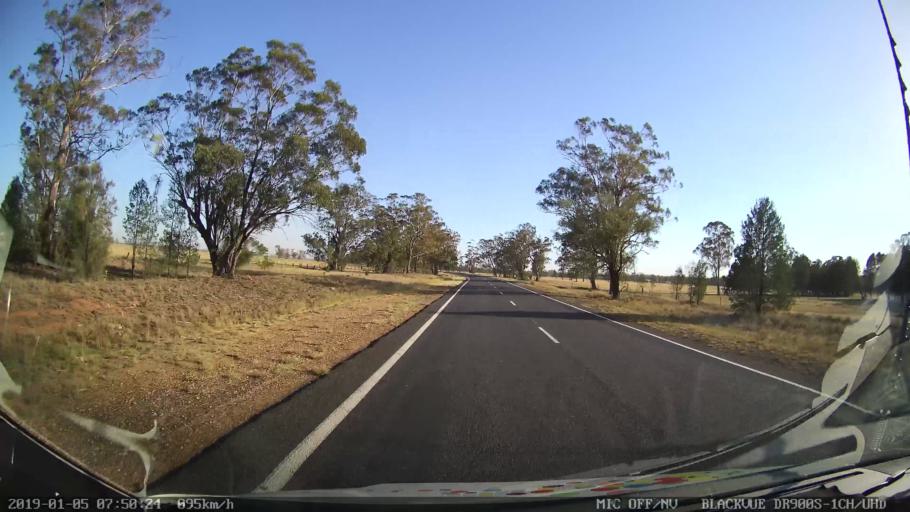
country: AU
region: New South Wales
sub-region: Gilgandra
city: Gilgandra
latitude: -31.7880
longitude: 148.6368
